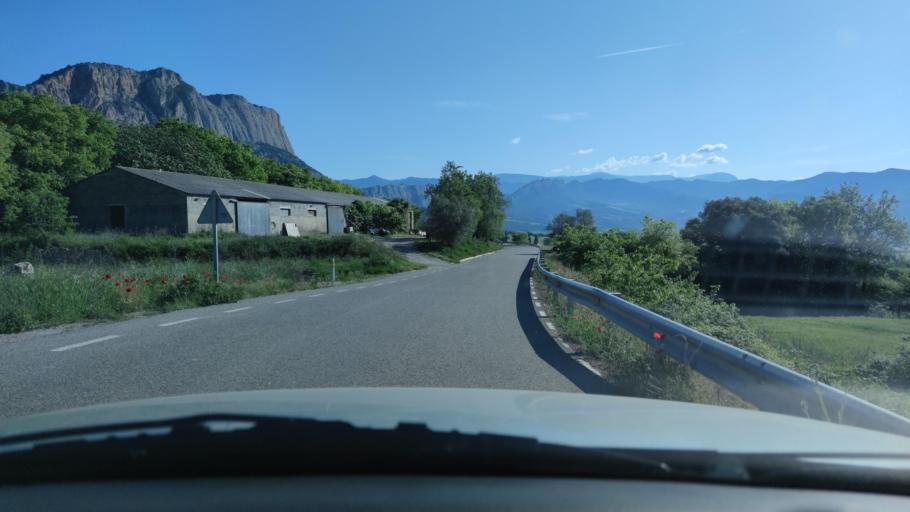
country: ES
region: Catalonia
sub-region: Provincia de Lleida
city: Oliana
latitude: 42.0611
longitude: 1.2735
